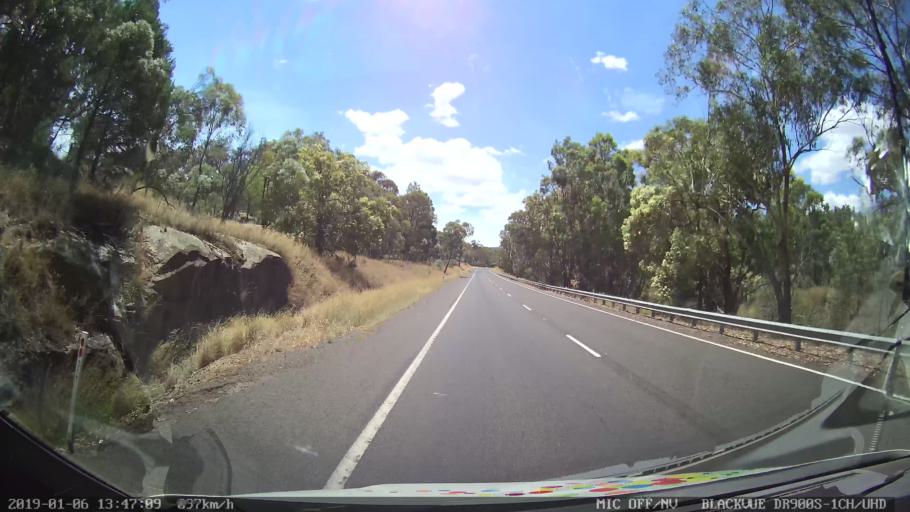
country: AU
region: New South Wales
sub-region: Tamworth Municipality
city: Kootingal
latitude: -30.9689
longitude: 151.1051
